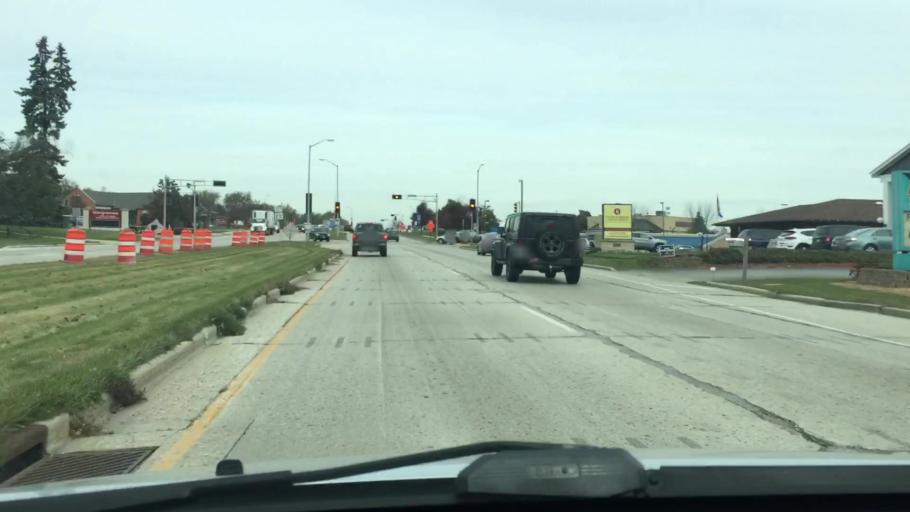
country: US
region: Wisconsin
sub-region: Waukesha County
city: New Berlin
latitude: 42.9738
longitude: -88.1085
